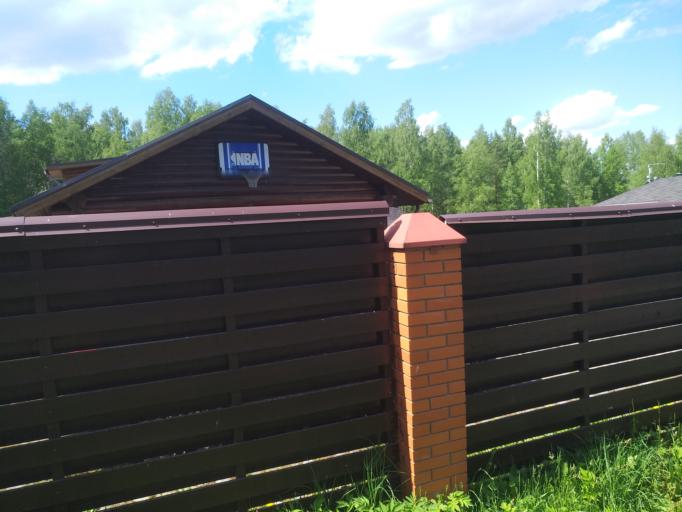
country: RU
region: Leningrad
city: Michurinskoye
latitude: 60.5866
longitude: 29.8797
